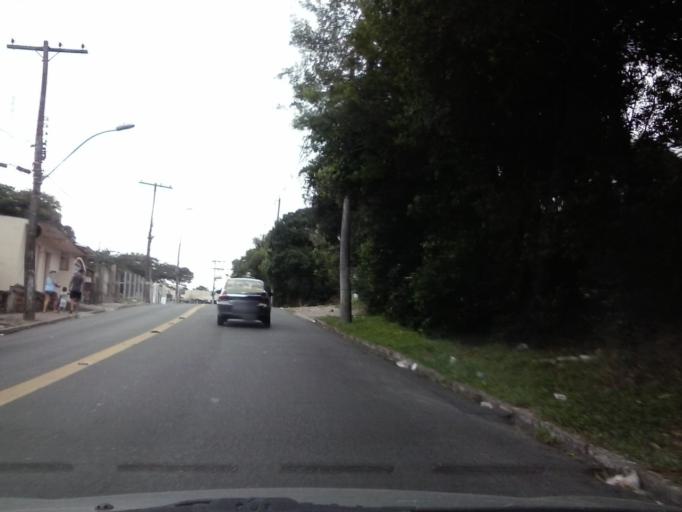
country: BR
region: Rio Grande do Sul
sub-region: Porto Alegre
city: Porto Alegre
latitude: -30.0933
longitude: -51.1793
